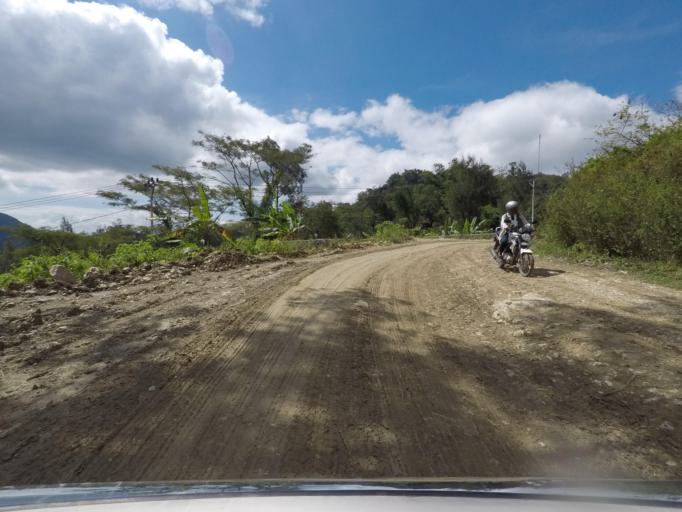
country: TL
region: Baucau
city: Venilale
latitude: -8.7244
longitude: 126.3680
